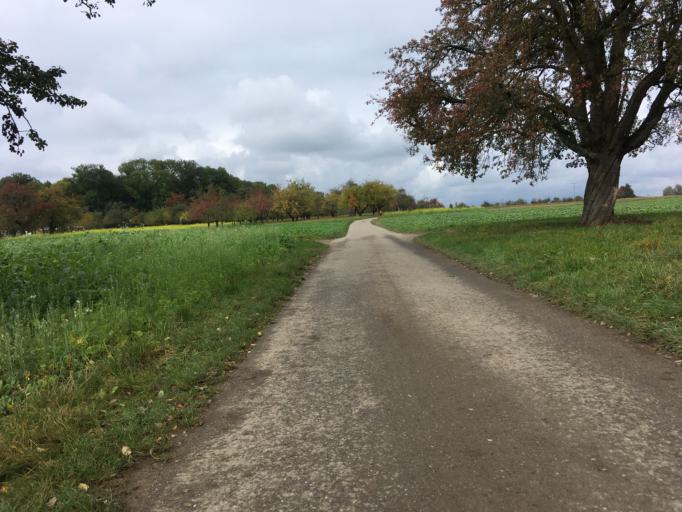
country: DE
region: Baden-Wuerttemberg
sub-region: Tuebingen Region
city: Gomaringen
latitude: 48.4879
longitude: 9.0946
